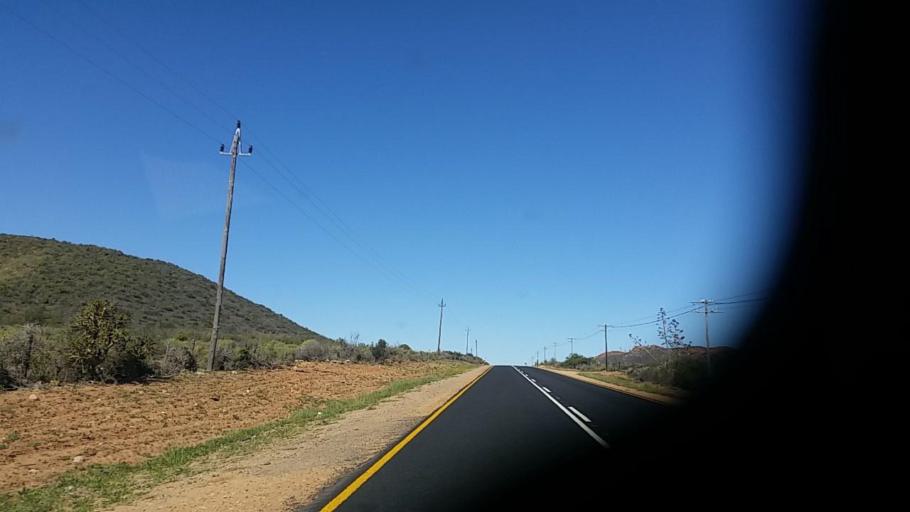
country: ZA
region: Western Cape
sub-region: Eden District Municipality
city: Oudtshoorn
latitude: -33.4875
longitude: 22.5785
